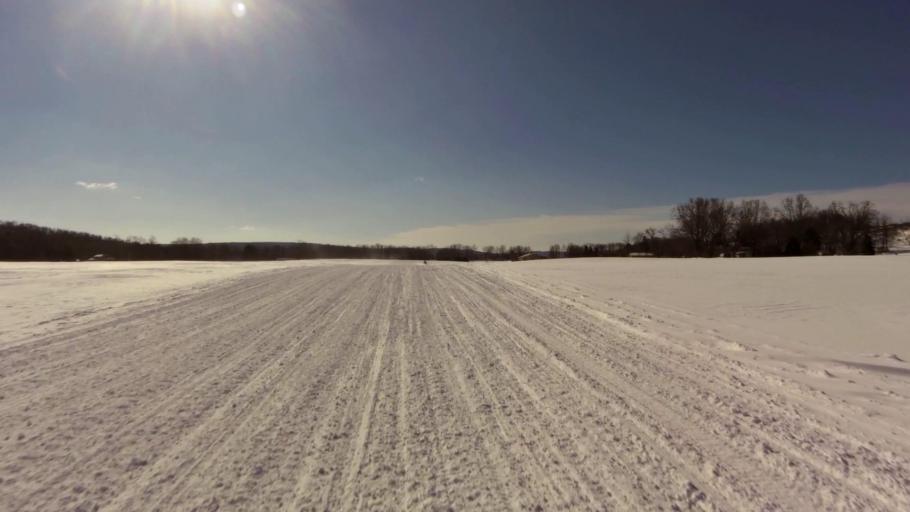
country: US
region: New York
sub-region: Cattaraugus County
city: Franklinville
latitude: 42.3837
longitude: -78.4717
